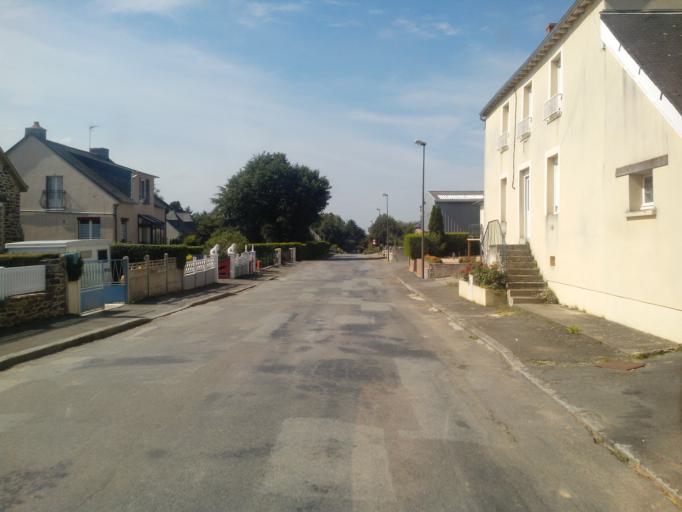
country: FR
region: Brittany
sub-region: Departement d'Ille-et-Vilaine
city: Gael
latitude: 48.1327
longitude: -2.2255
